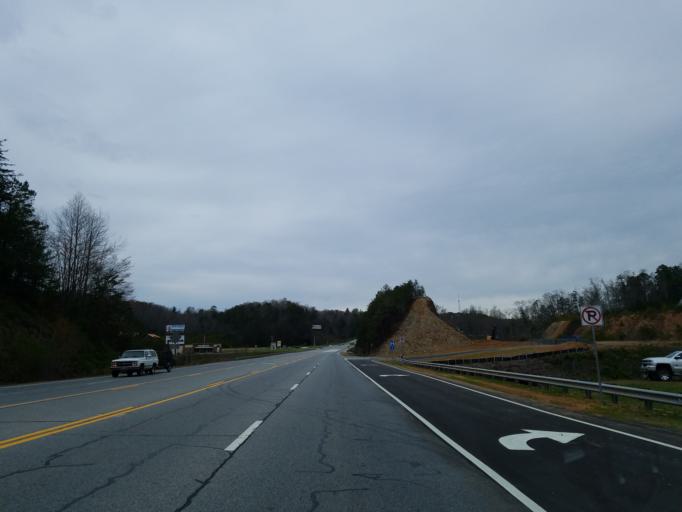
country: US
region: Georgia
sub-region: Fannin County
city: Blue Ridge
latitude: 34.8490
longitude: -84.3366
